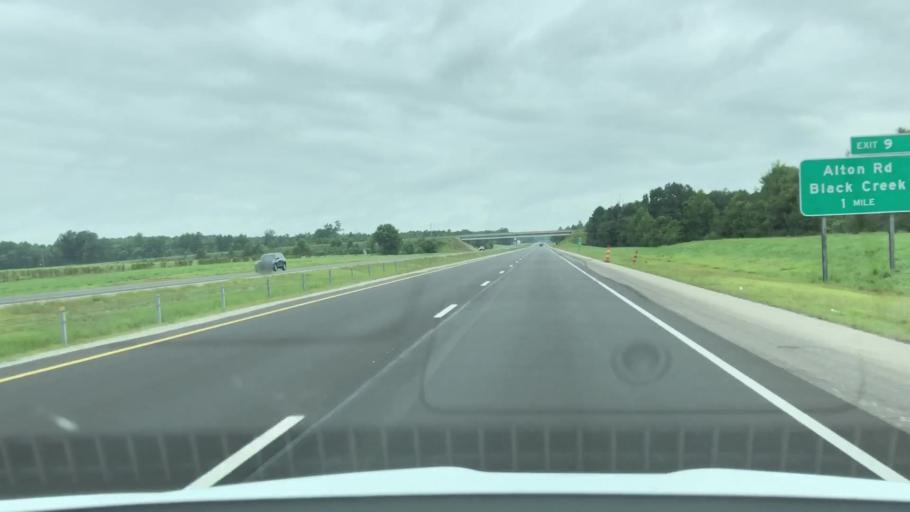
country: US
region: North Carolina
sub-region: Wilson County
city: Lucama
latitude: 35.6013
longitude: -77.9806
